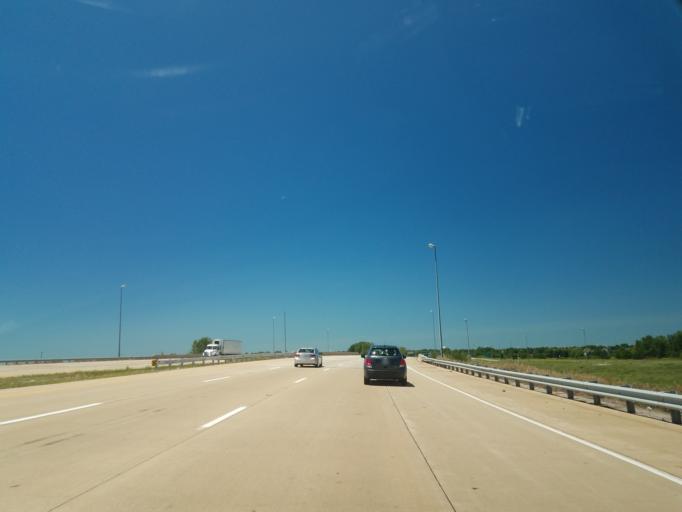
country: US
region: Illinois
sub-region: McLean County
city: Normal
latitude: 40.5378
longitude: -88.9473
